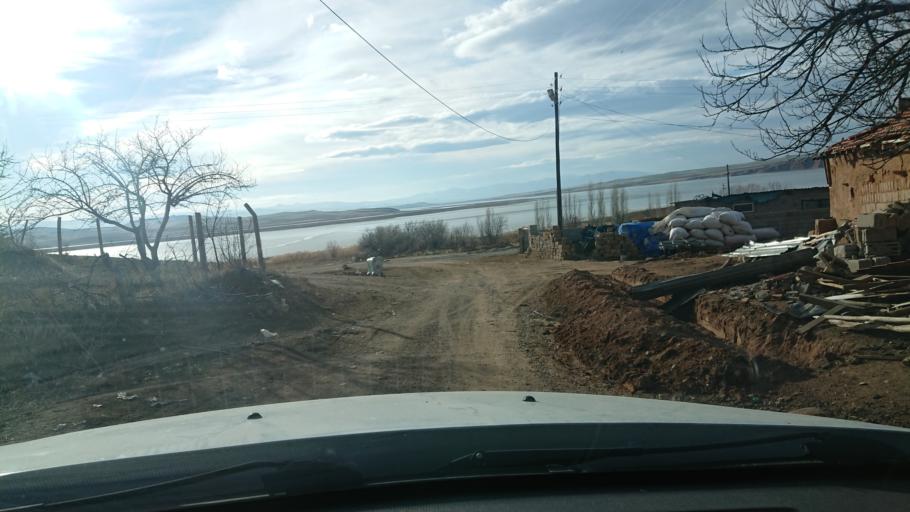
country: TR
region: Aksaray
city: Sariyahsi
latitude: 39.0530
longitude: 33.9761
